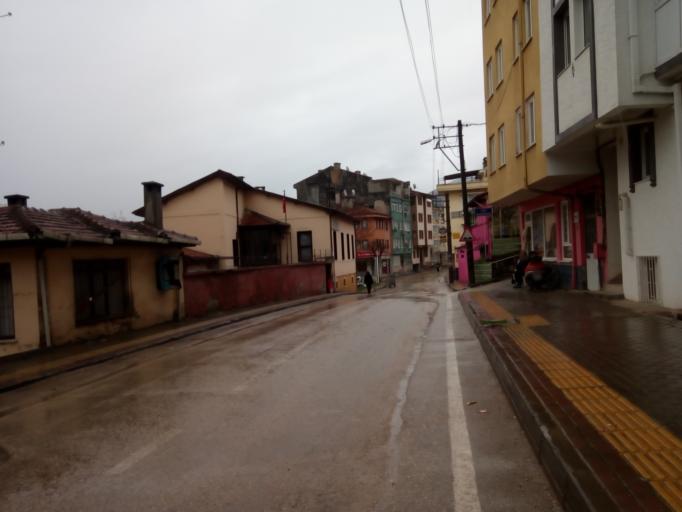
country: TR
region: Bursa
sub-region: Osmangazi
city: Bursa
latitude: 40.1796
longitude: 29.0577
